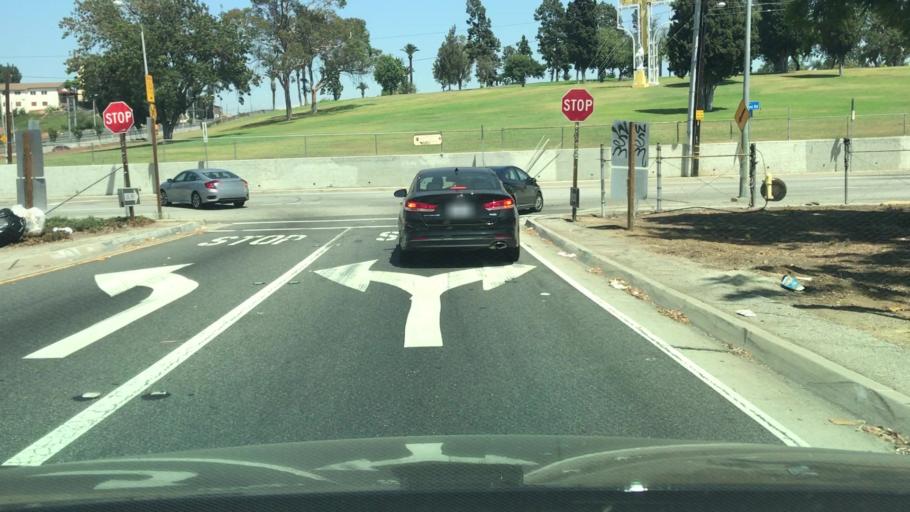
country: US
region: California
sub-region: Los Angeles County
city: East Los Angeles
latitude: 34.0327
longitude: -118.1806
